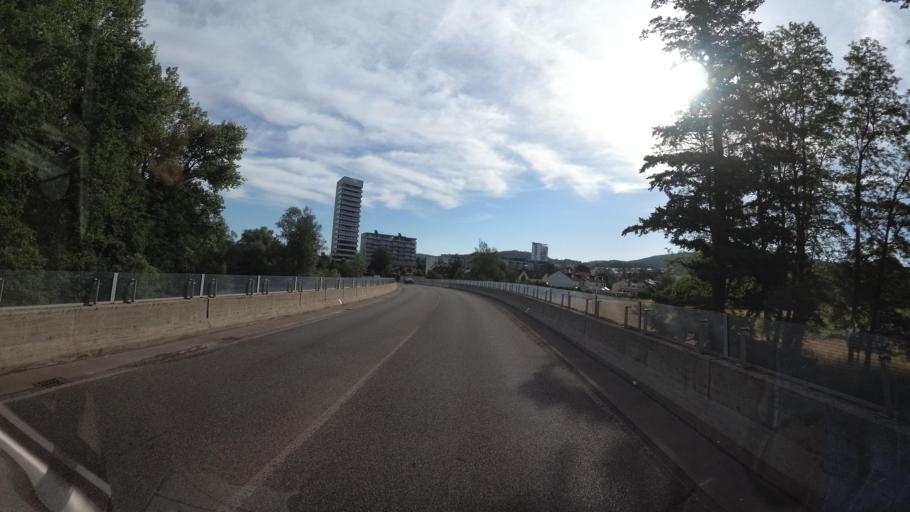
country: CH
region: Basel-City
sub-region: Basel-Stadt
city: Riehen
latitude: 47.5955
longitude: 7.6491
